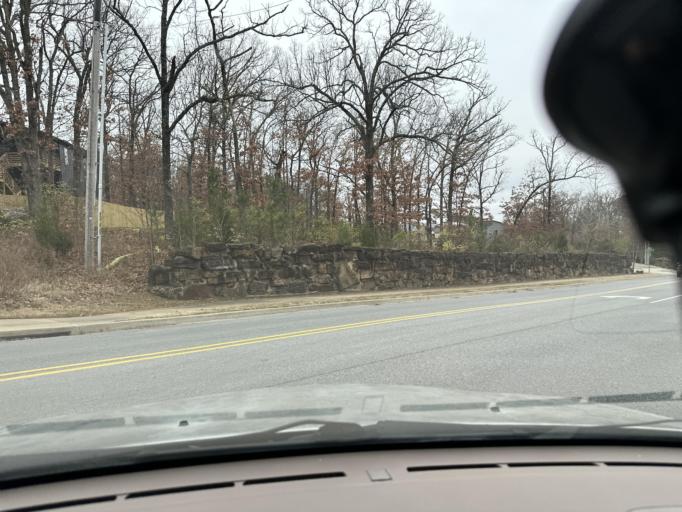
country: US
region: Arkansas
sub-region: Washington County
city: Fayetteville
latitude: 36.0950
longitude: -94.1486
